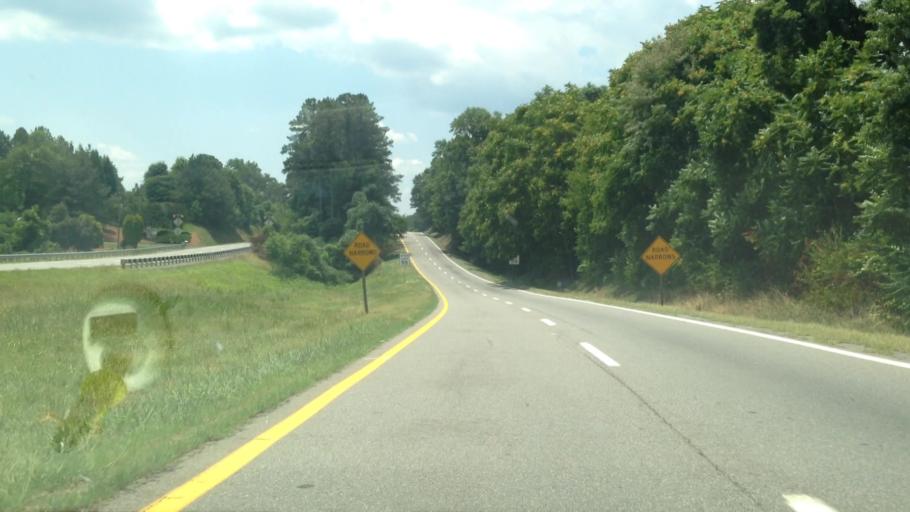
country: US
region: Virginia
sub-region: Henry County
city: Horse Pasture
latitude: 36.5704
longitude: -79.8728
